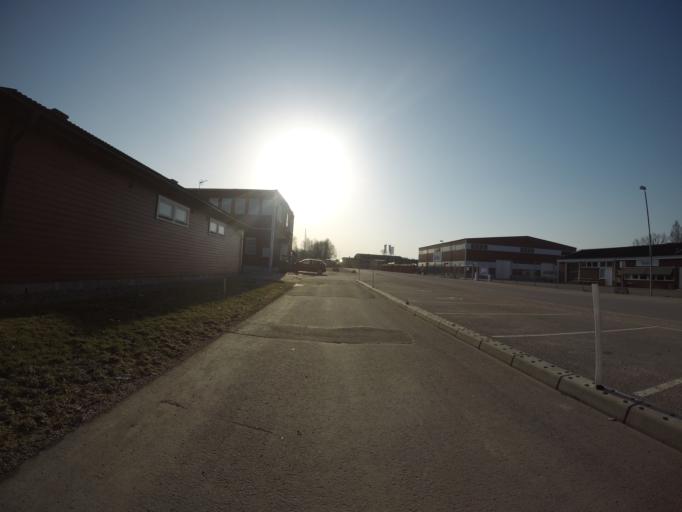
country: SE
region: Vaestmanland
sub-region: Kungsors Kommun
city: Kungsoer
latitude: 59.4292
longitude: 16.1095
